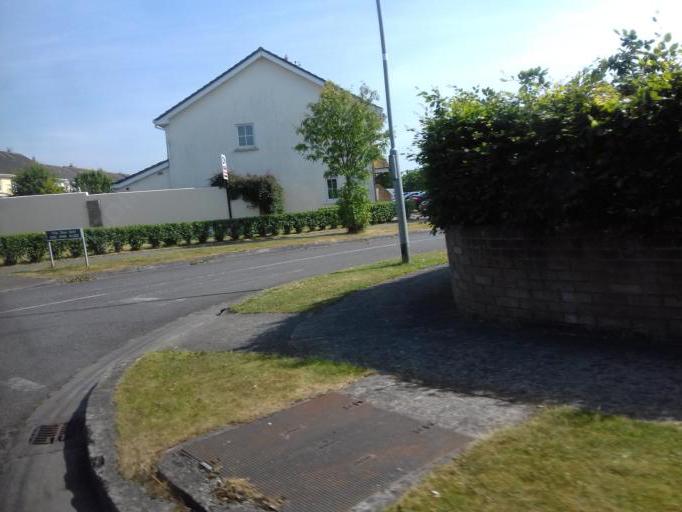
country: IE
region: Leinster
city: Lusk
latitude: 53.5256
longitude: -6.1806
